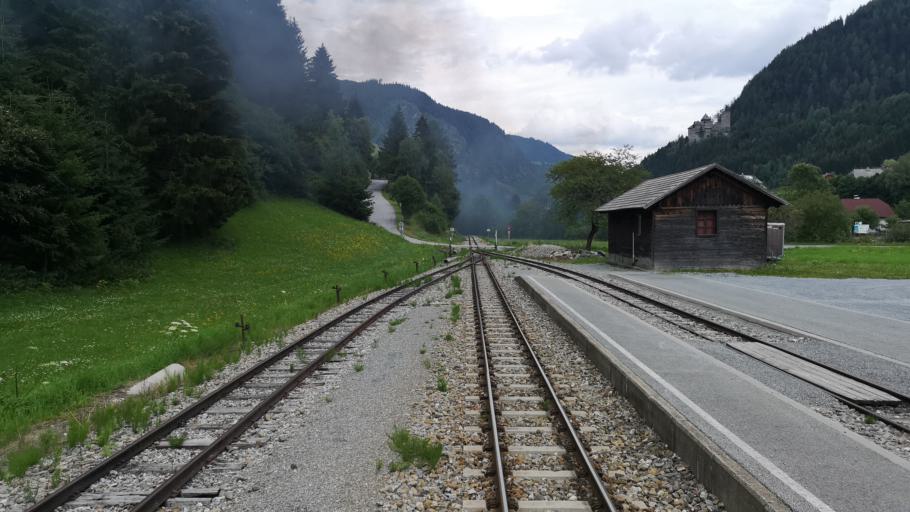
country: AT
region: Salzburg
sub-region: Politischer Bezirk Tamsweg
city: Ramingstein
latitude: 47.0753
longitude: 13.8305
